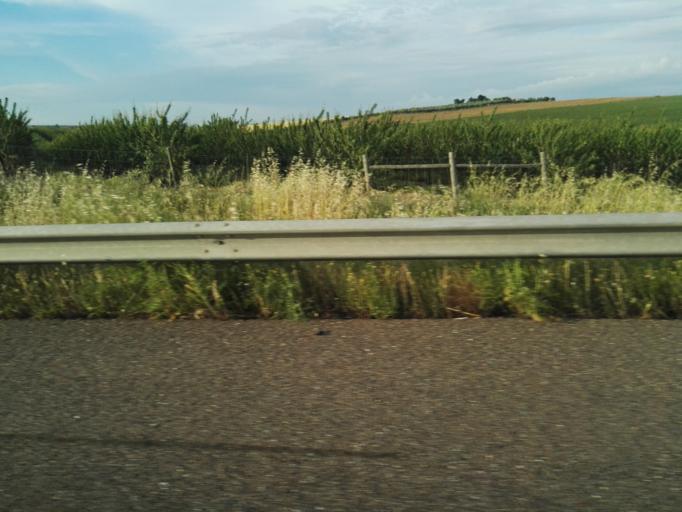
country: PT
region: Portalegre
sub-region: Elvas
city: Elvas
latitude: 38.8920
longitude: -7.1162
